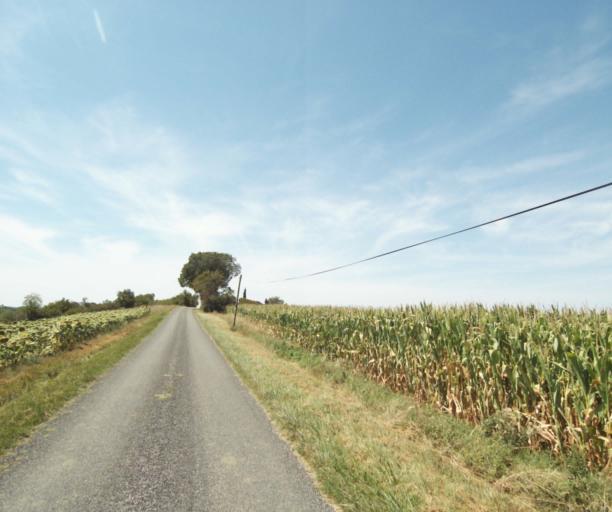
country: FR
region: Midi-Pyrenees
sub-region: Departement de l'Ariege
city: Lezat-sur-Leze
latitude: 43.2526
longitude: 1.3236
